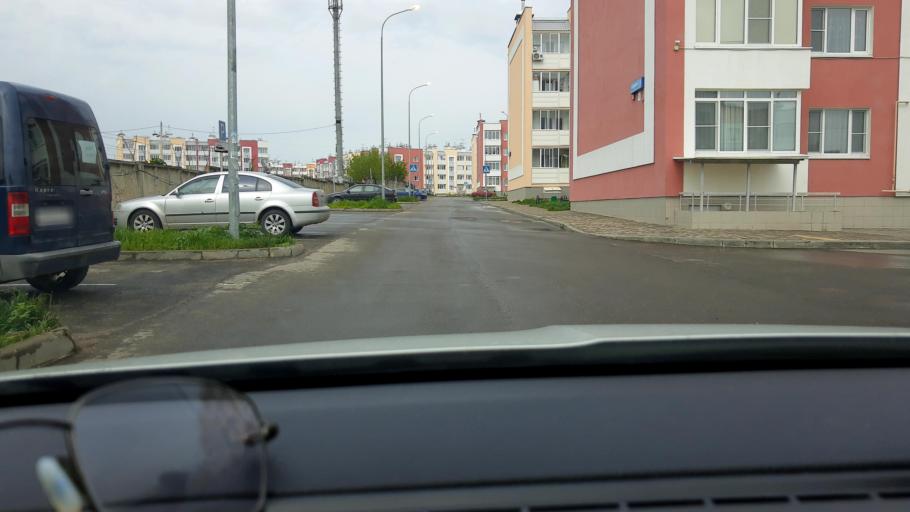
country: RU
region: Moskovskaya
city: Dedovsk
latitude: 55.8393
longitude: 37.1320
